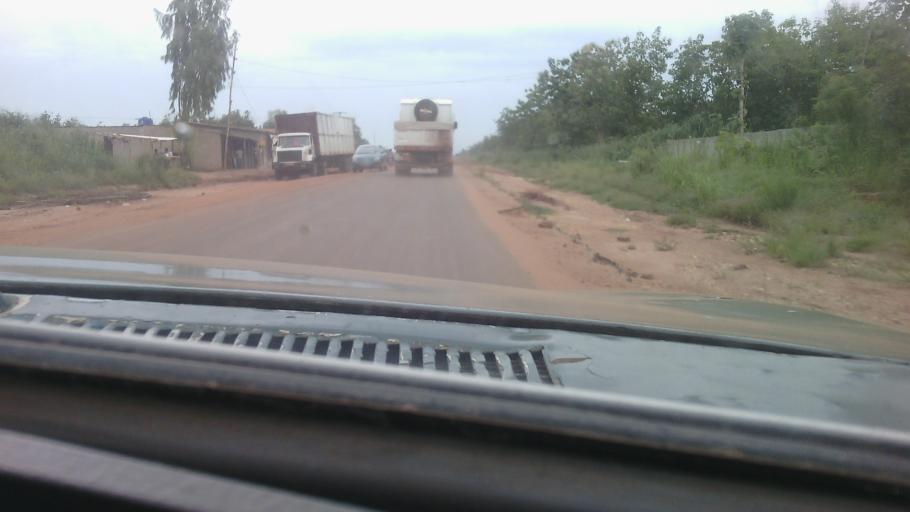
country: BJ
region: Mono
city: Come
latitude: 6.5040
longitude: 1.8349
